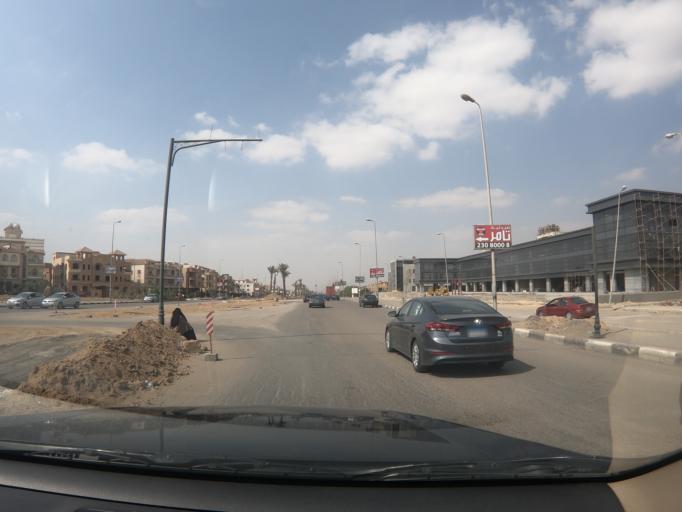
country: EG
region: Muhafazat al Qalyubiyah
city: Al Khankah
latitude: 30.0478
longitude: 31.4750
